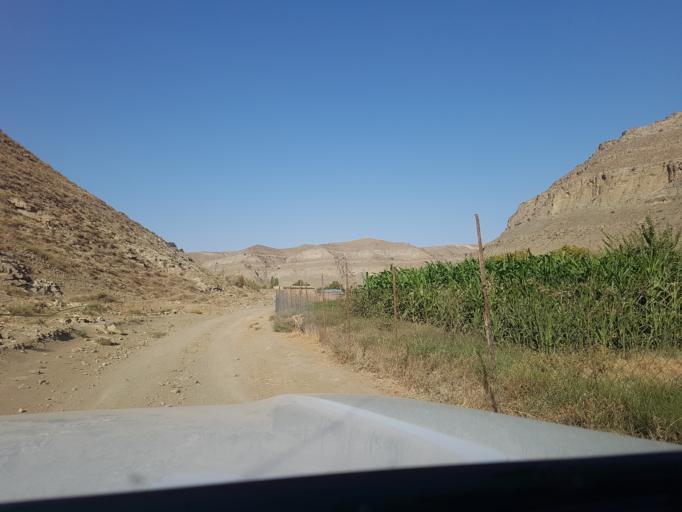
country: TM
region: Balkan
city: Magtymguly
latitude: 38.3000
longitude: 56.7531
